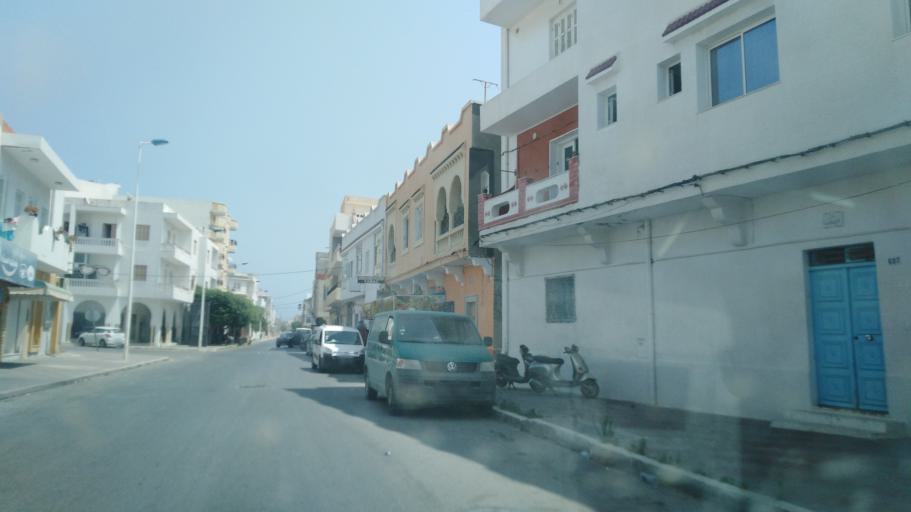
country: TN
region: Al Mahdiyah
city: Mahdia
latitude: 35.5129
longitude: 11.0457
